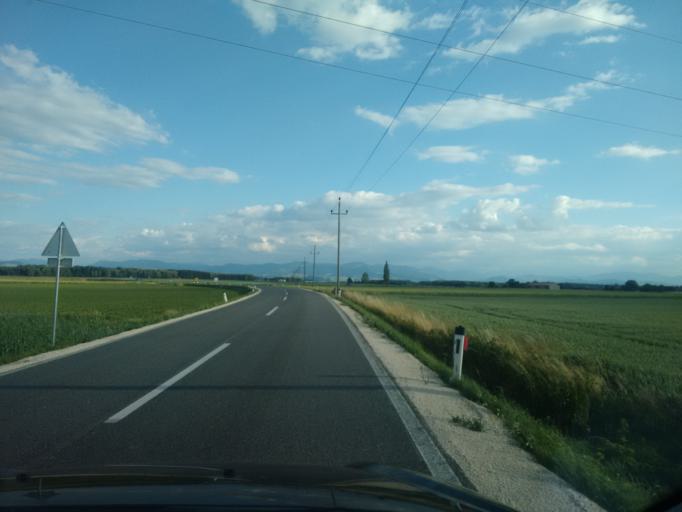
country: AT
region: Upper Austria
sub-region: Politischer Bezirk Steyr-Land
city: Sierning
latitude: 48.0912
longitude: 14.3185
